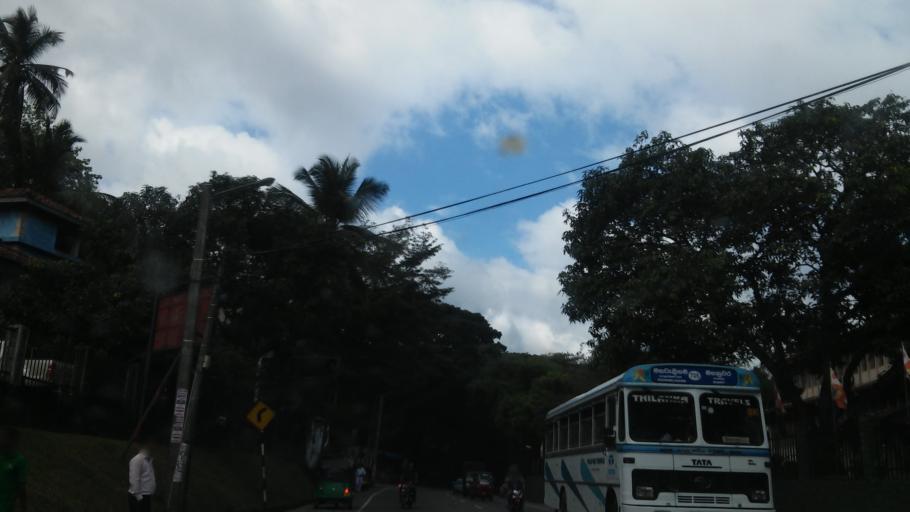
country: LK
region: Central
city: Kandy
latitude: 7.2700
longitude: 80.6047
